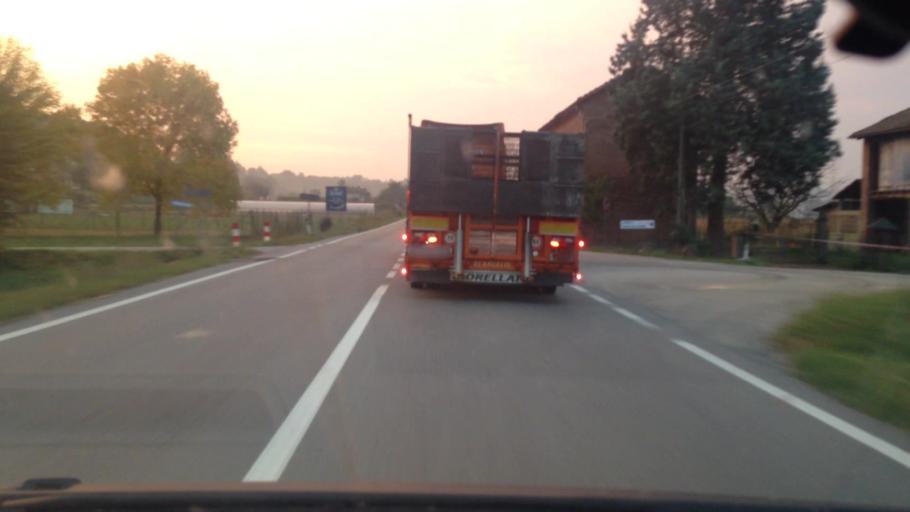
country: IT
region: Piedmont
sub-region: Provincia di Asti
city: Rocca d'Arazzo
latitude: 44.9038
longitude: 8.2879
